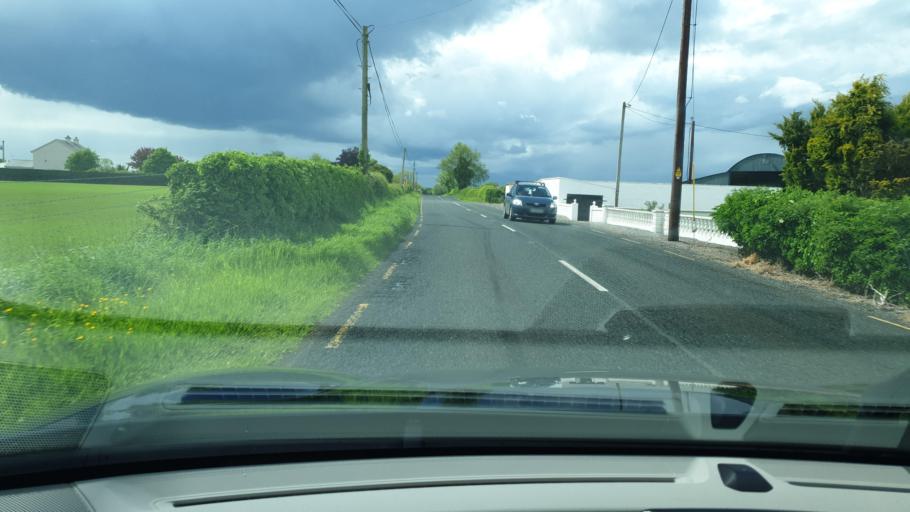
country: IE
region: Leinster
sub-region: Uibh Fhaili
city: Clara
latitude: 53.2358
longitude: -7.6482
